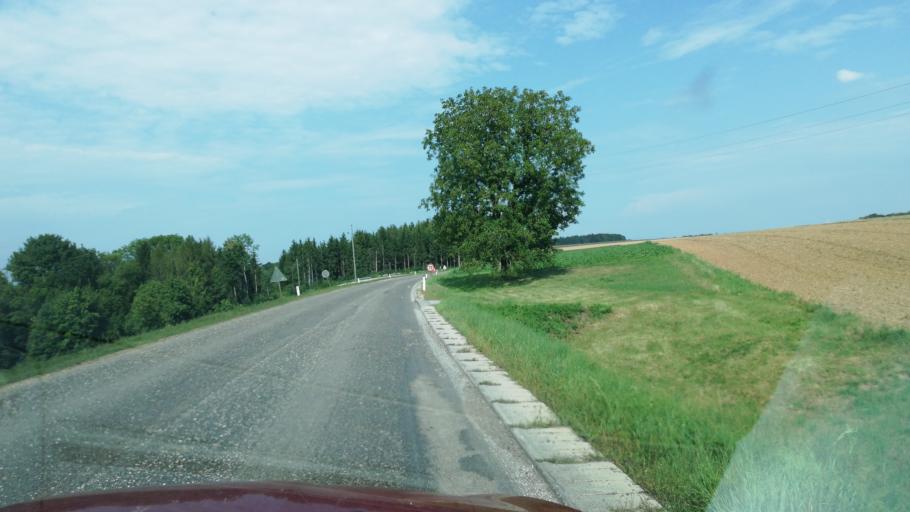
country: AT
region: Upper Austria
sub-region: Politischer Bezirk Steyr-Land
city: Sierning
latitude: 48.1054
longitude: 14.3196
